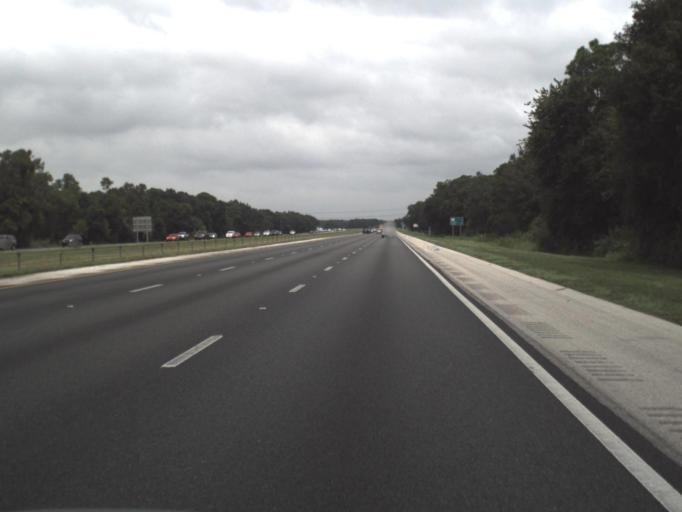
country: US
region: Florida
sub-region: Manatee County
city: Samoset
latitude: 27.4533
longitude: -82.4590
